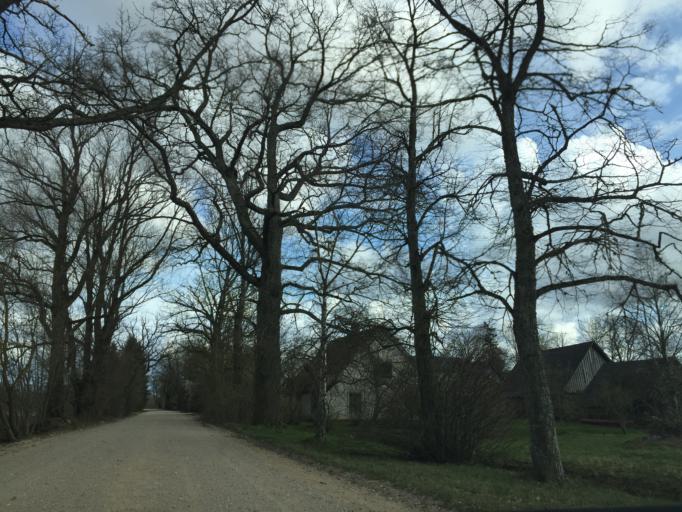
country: LV
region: Limbazu Rajons
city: Limbazi
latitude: 57.6139
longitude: 24.7373
